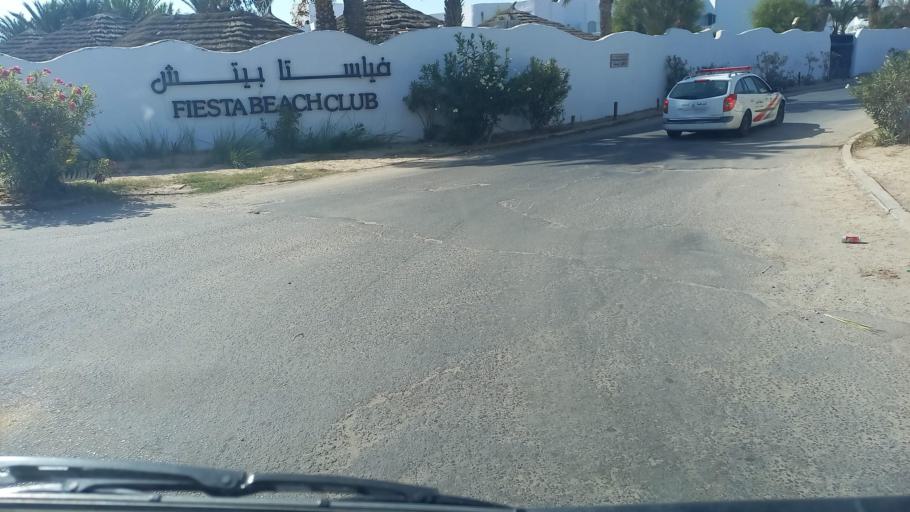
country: TN
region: Madanin
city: Midoun
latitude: 33.8508
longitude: 10.9889
